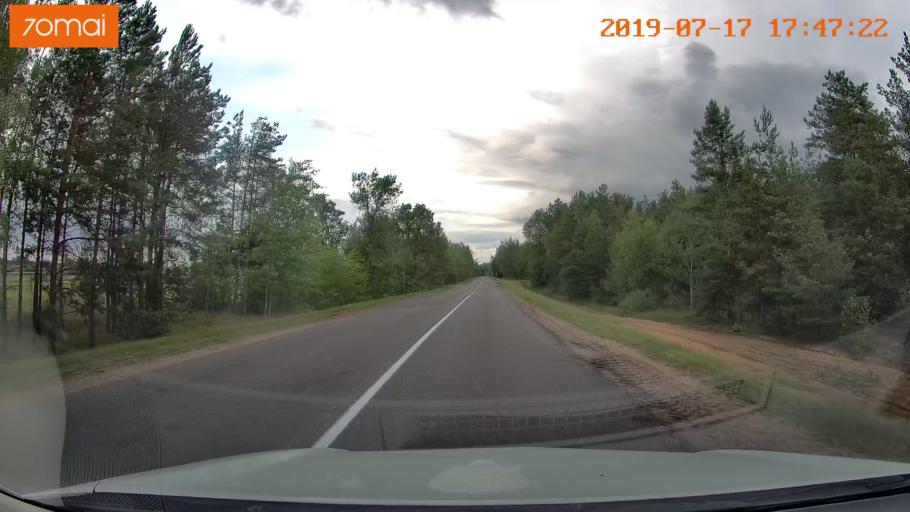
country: BY
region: Mogilev
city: Hlusha
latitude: 53.1098
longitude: 28.8289
